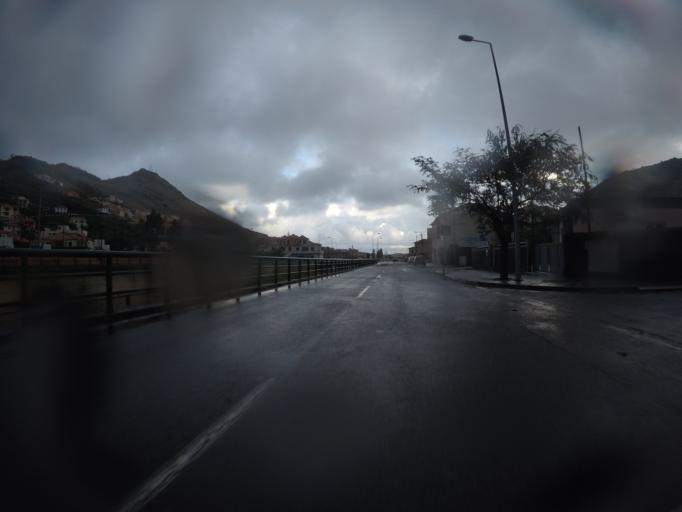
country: PT
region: Madeira
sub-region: Machico
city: Machico
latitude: 32.7248
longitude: -16.7712
